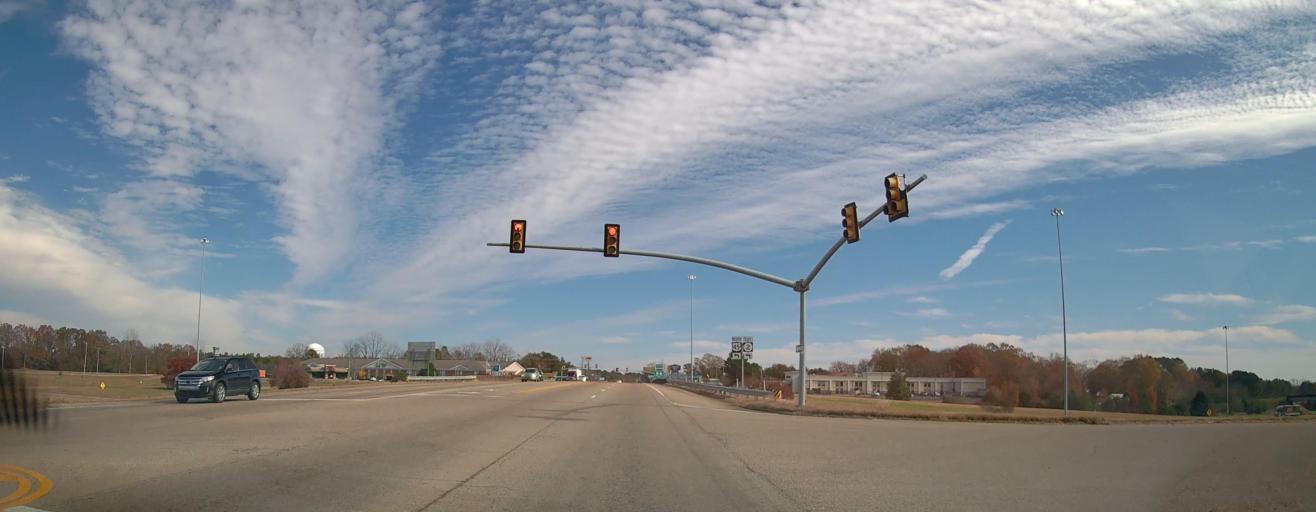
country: US
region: Mississippi
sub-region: Alcorn County
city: Corinth
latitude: 34.9309
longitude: -88.5490
